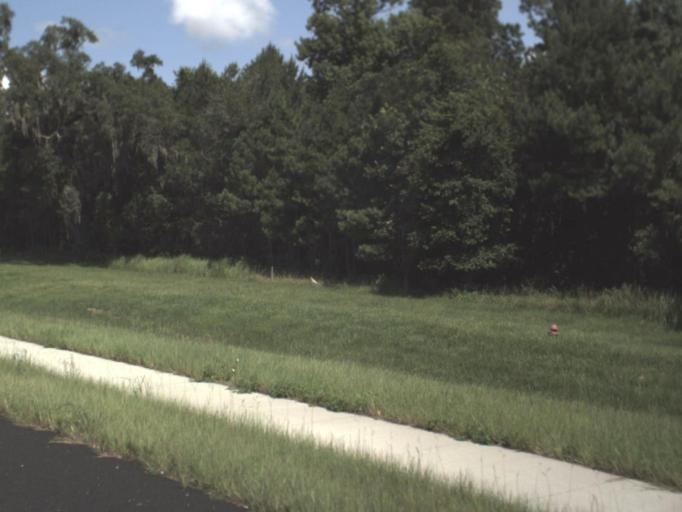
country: US
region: Florida
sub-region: Hernando County
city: South Brooksville
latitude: 28.5414
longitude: -82.4392
